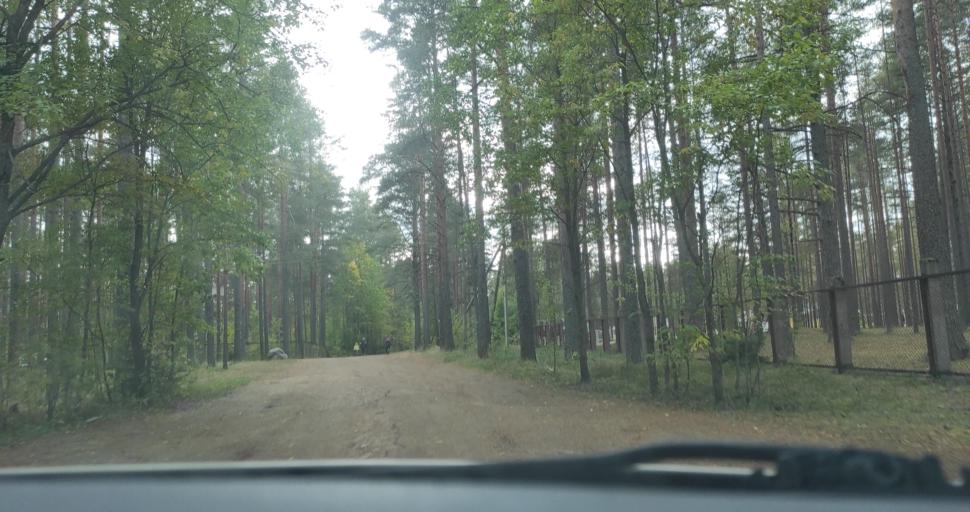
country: RU
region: Leningrad
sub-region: Vsevolzhskij Rajon
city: Vaskelovo
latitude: 60.4074
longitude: 30.3264
